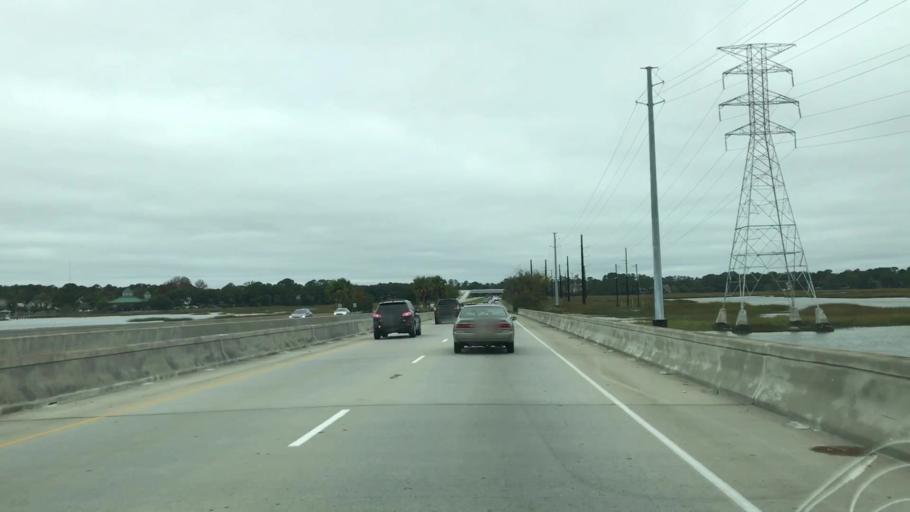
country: US
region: South Carolina
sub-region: Beaufort County
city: Hilton Head Island
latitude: 32.2311
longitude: -80.7926
